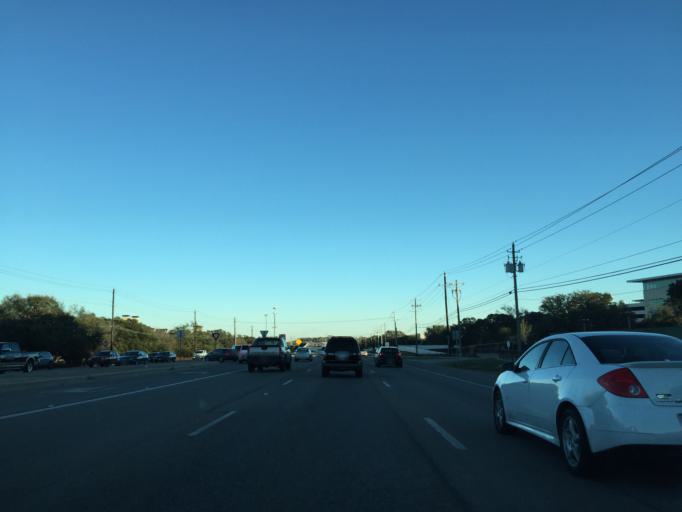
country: US
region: Texas
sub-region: Williamson County
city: Jollyville
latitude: 30.4363
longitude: -97.7347
